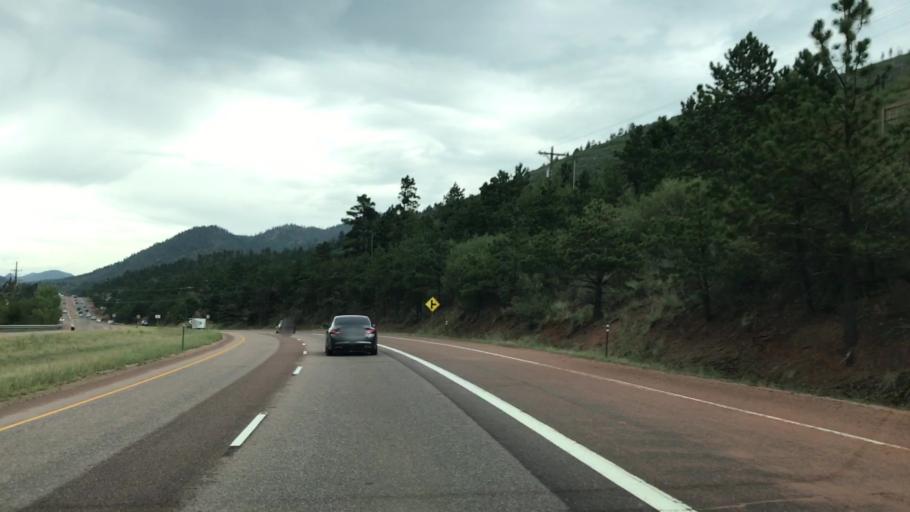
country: US
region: Colorado
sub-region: El Paso County
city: Cascade-Chipita Park
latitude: 38.9068
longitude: -104.9706
